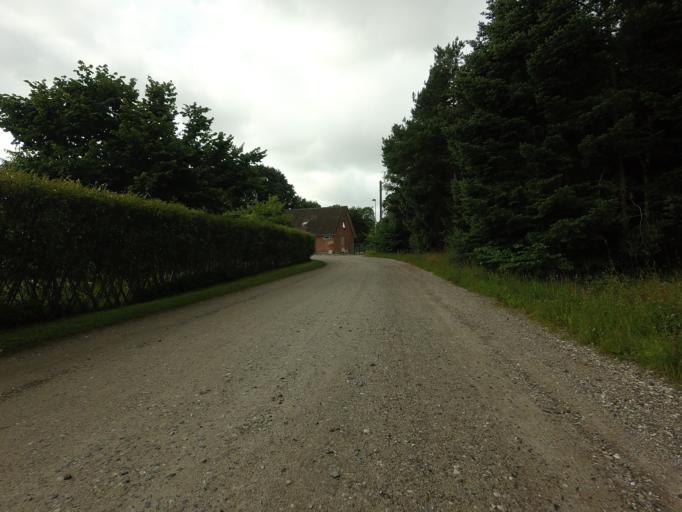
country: DK
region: Central Jutland
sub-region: Randers Kommune
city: Langa
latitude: 56.3855
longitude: 9.8981
